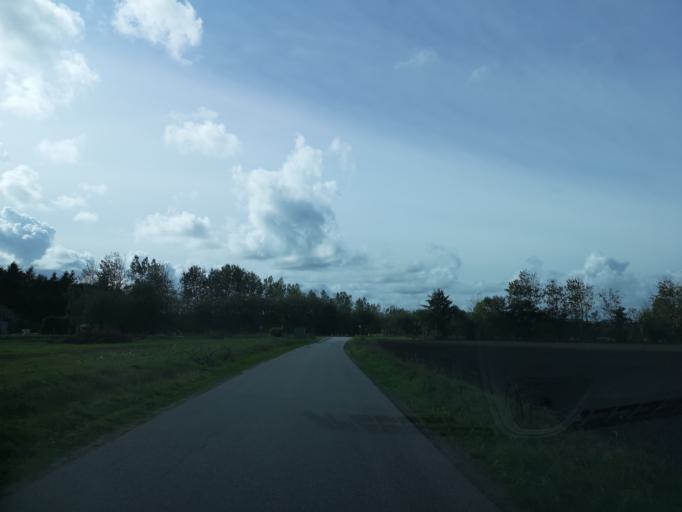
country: DK
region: Central Jutland
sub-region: Ringkobing-Skjern Kommune
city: Skjern
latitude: 55.9435
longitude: 8.5293
